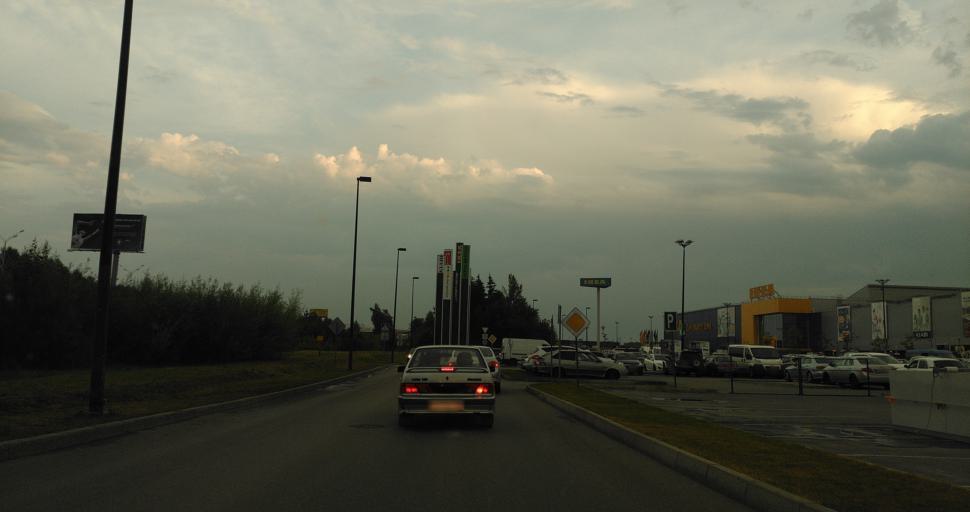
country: RU
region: Bashkortostan
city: Ufa
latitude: 54.6756
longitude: 55.9324
